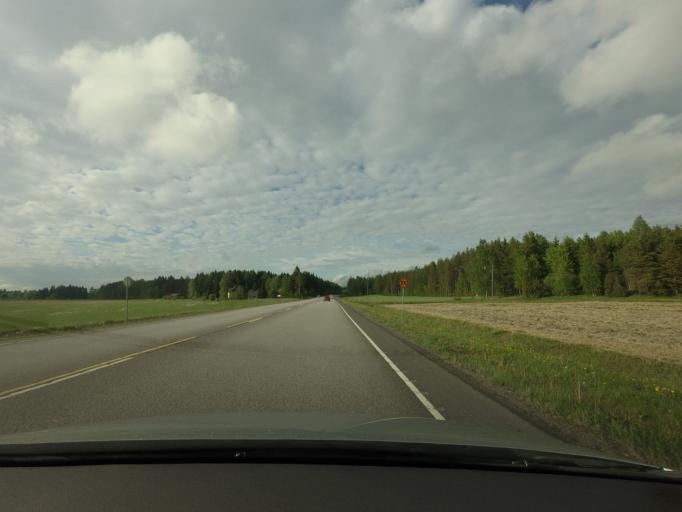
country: FI
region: Uusimaa
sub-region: Loviisa
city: Lapinjaervi
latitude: 60.6753
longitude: 26.2543
